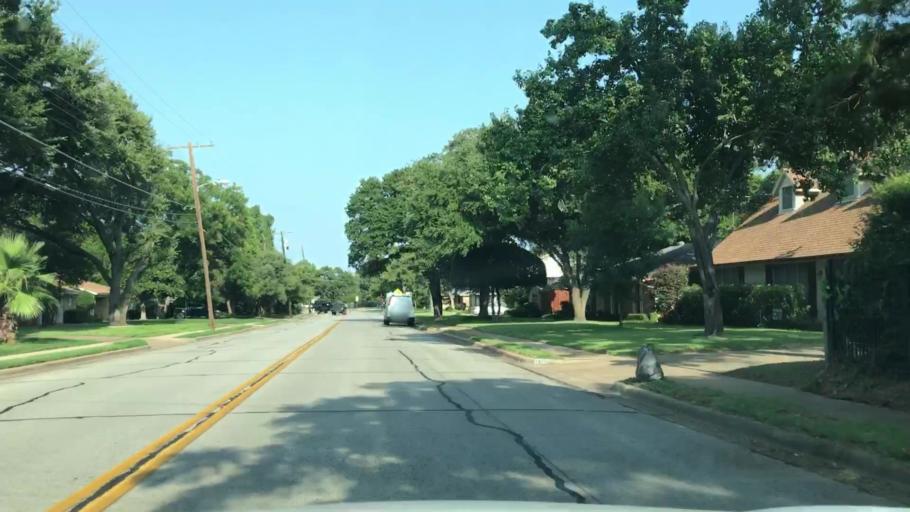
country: US
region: Texas
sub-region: Dallas County
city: Irving
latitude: 32.8230
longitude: -96.9278
